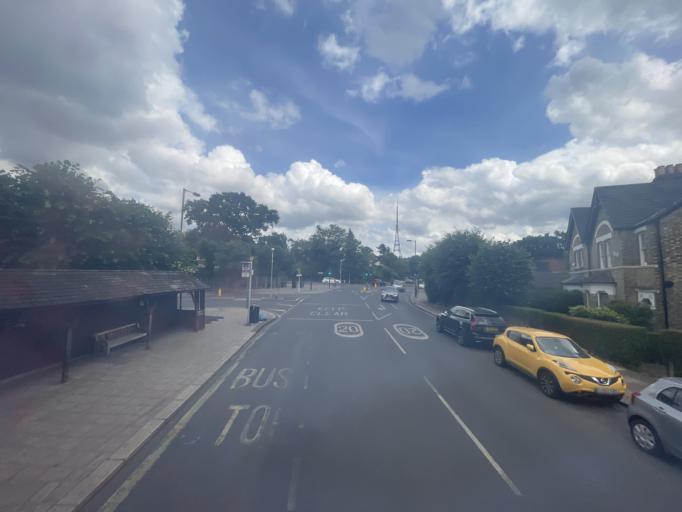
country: GB
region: England
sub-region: Greater London
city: Thornton Heath
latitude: 51.4288
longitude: -0.0867
